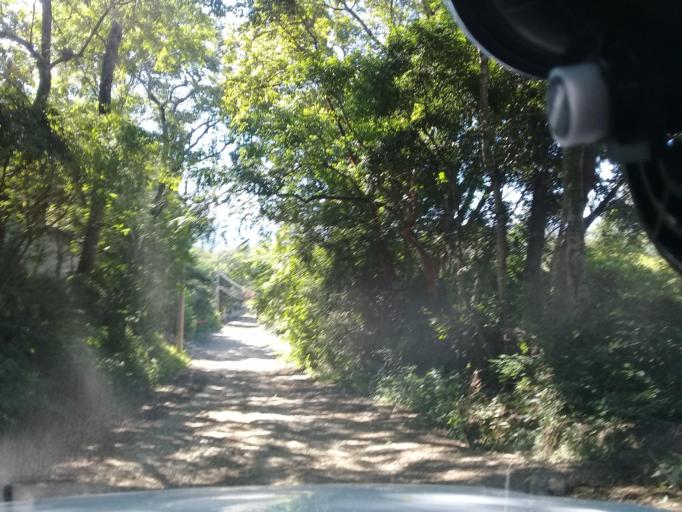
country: MX
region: Hidalgo
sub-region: Huejutla de Reyes
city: Huejutla de Reyes
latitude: 21.1625
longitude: -98.4130
